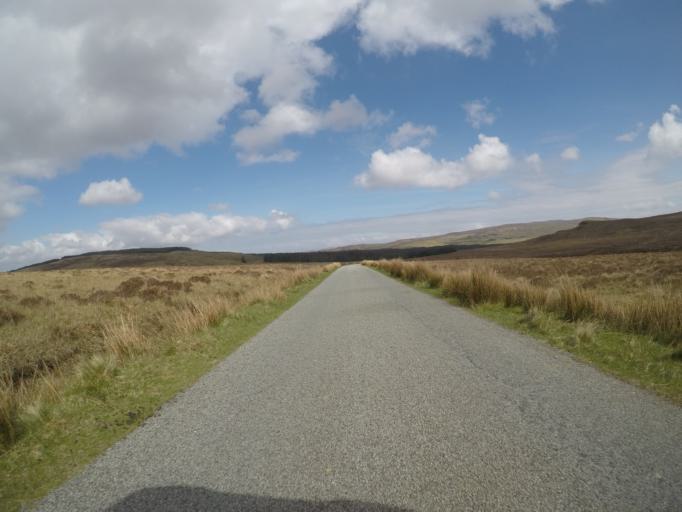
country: GB
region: Scotland
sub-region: Highland
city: Isle of Skye
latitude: 57.4029
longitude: -6.3325
